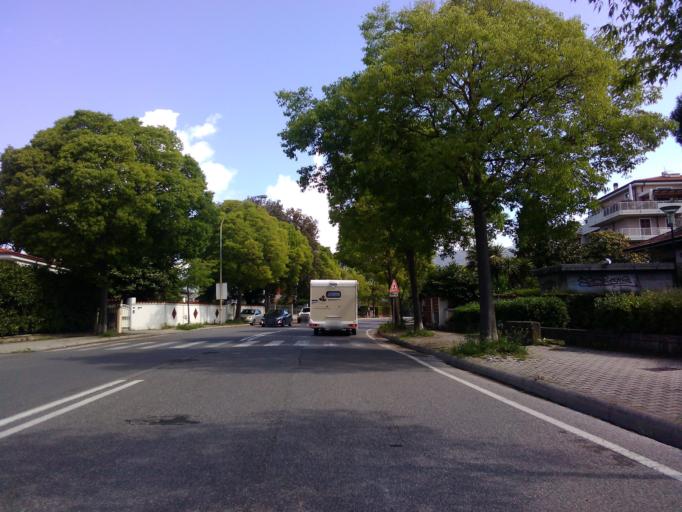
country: IT
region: Tuscany
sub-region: Provincia di Massa-Carrara
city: Marina di Carrara
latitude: 44.0479
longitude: 10.0338
